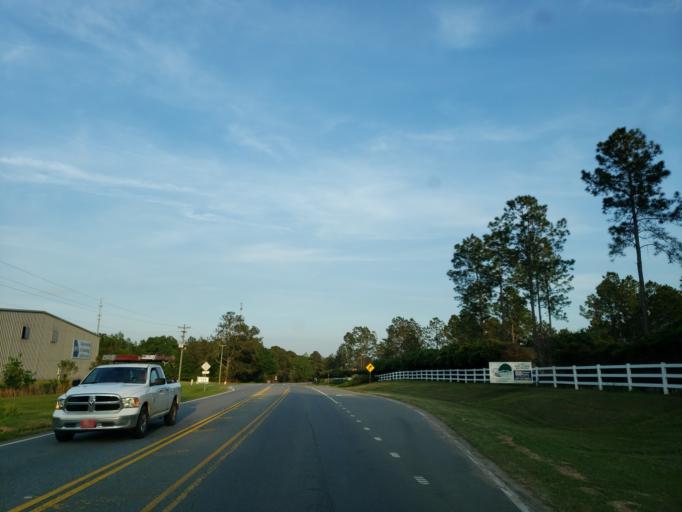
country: US
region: Georgia
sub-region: Lowndes County
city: Hahira
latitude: 30.9946
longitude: -83.3990
